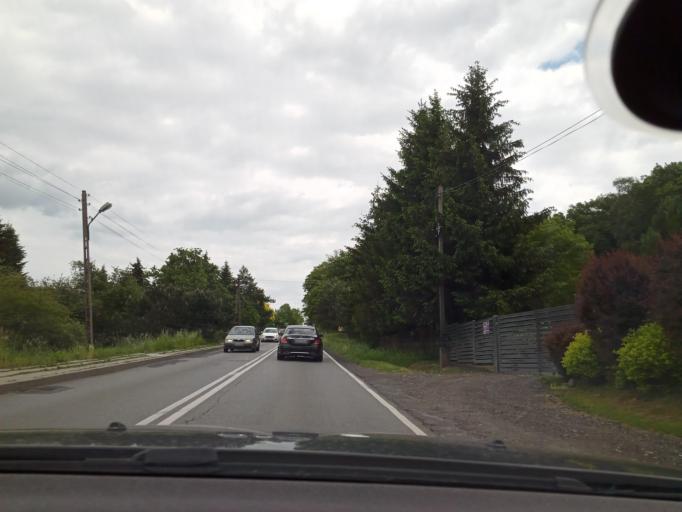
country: PL
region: Lesser Poland Voivodeship
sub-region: Powiat wielicki
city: Tomaszkowice
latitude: 49.9730
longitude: 20.1139
